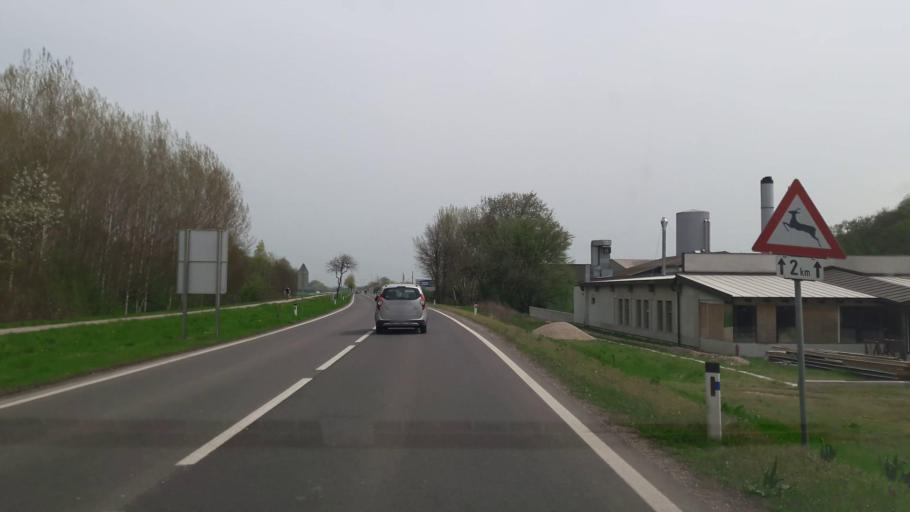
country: AT
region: Lower Austria
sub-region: Politischer Bezirk Bruck an der Leitha
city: Wolfsthal
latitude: 48.1292
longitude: 17.0232
